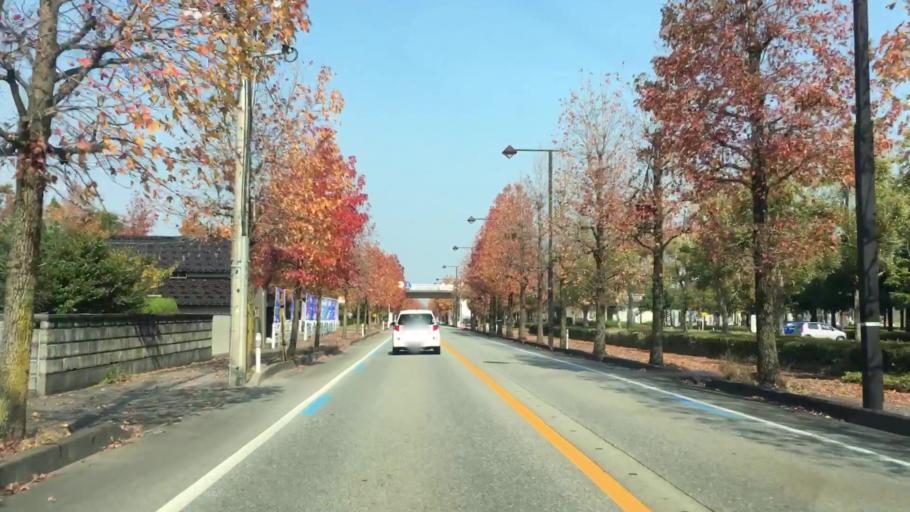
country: JP
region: Toyama
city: Toyama-shi
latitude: 36.6253
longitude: 137.1935
